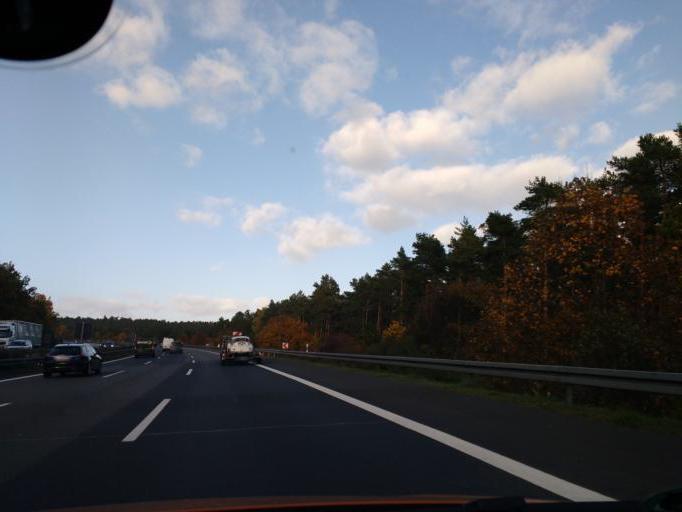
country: DE
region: Brandenburg
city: Grunheide
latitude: 52.4416
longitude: 13.8008
